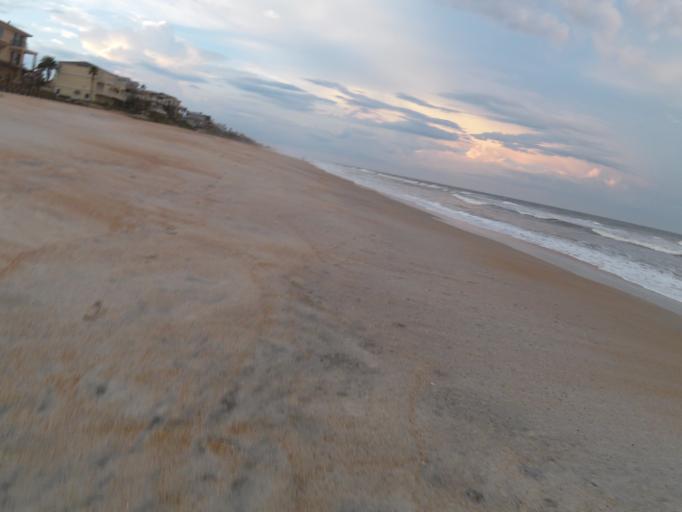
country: US
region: Florida
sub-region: Saint Johns County
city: Villano Beach
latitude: 29.9790
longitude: -81.3115
